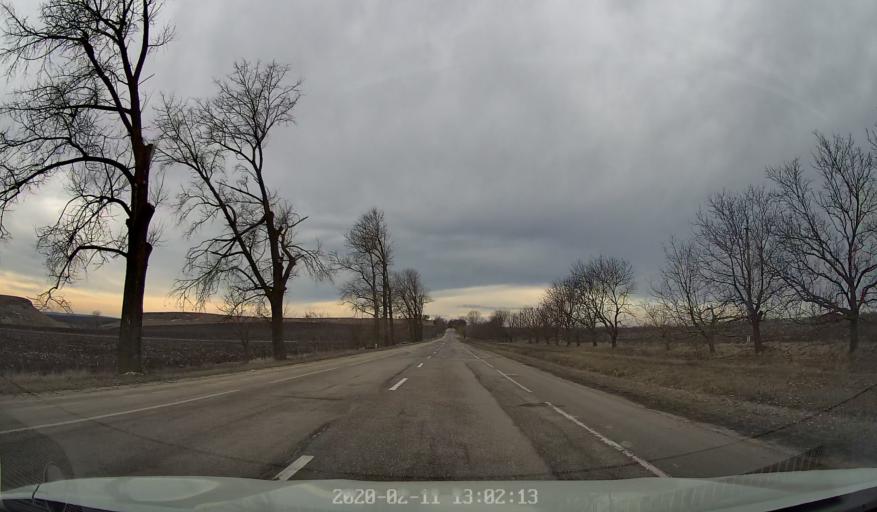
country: MD
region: Briceni
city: Briceni
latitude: 48.3164
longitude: 26.9859
